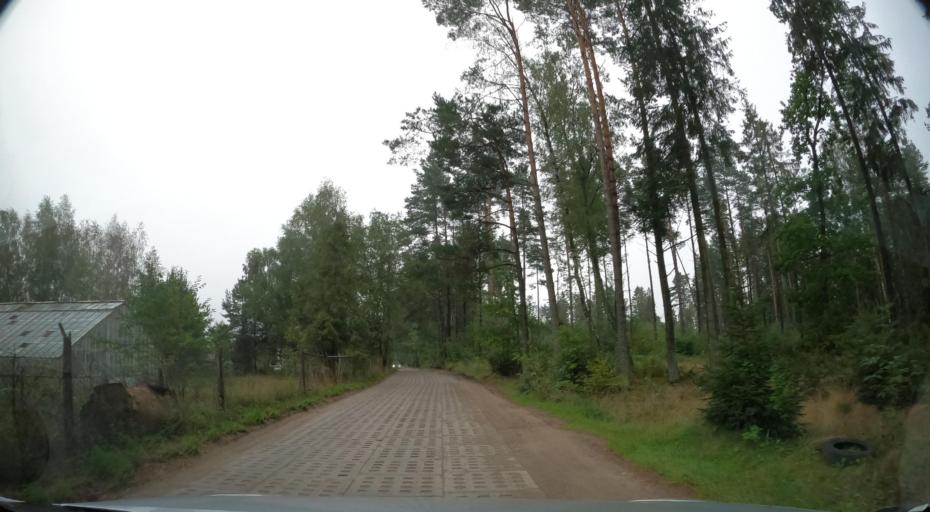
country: PL
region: Pomeranian Voivodeship
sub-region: Powiat kartuski
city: Chwaszczyno
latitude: 54.4177
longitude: 18.4308
